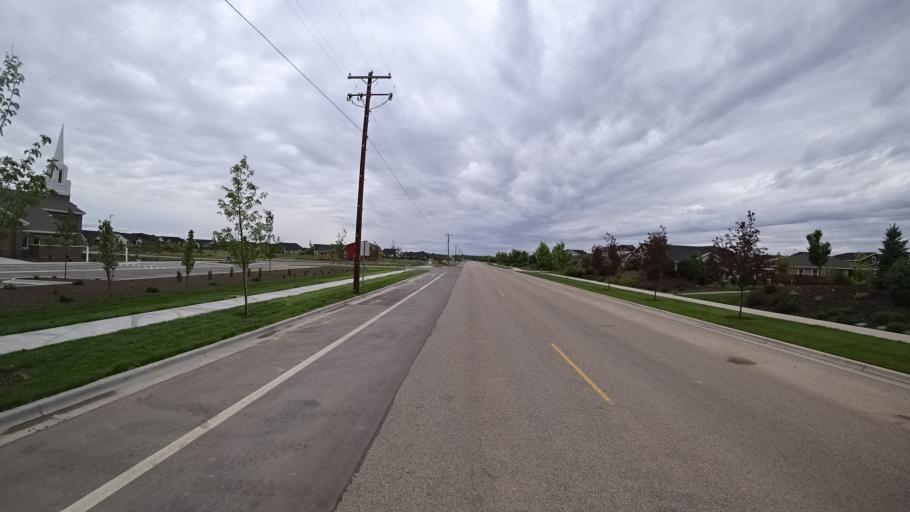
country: US
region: Idaho
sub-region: Ada County
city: Eagle
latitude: 43.7126
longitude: -116.4235
